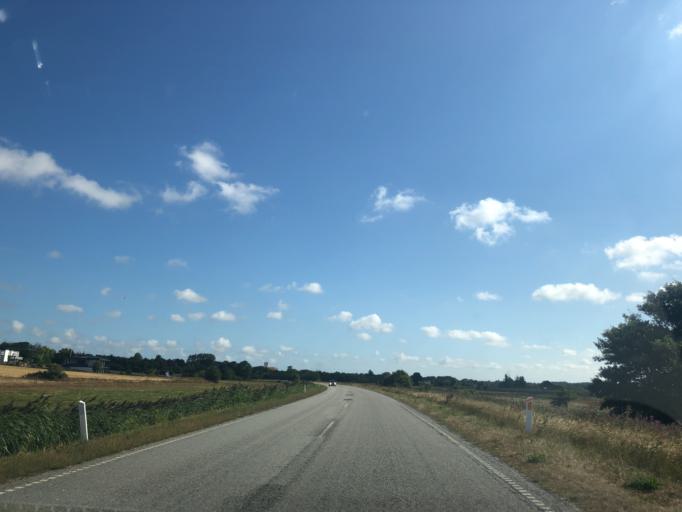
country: DK
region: North Denmark
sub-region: Morso Kommune
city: Nykobing Mors
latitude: 57.0193
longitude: 8.9873
